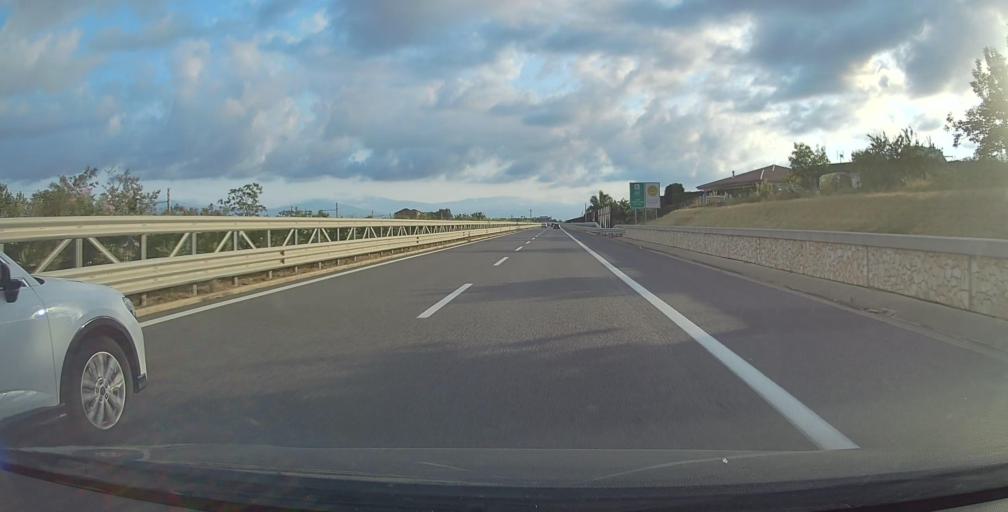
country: IT
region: Calabria
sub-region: Provincia di Catanzaro
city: Acconia
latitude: 38.8320
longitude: 16.2562
